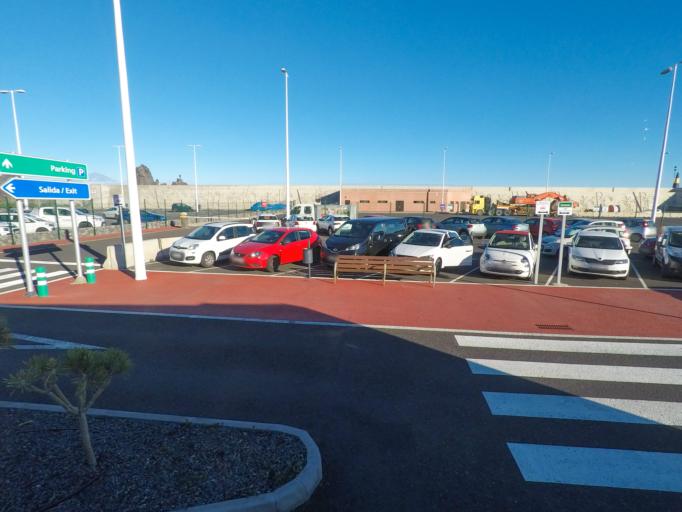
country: ES
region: Canary Islands
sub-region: Provincia de Santa Cruz de Tenerife
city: San Sebastian de la Gomera
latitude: 28.0889
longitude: -17.1063
